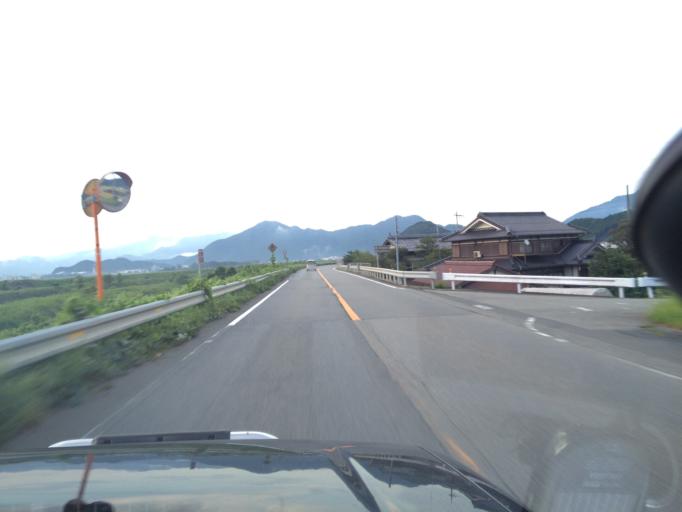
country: JP
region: Hyogo
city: Nishiwaki
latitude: 35.1422
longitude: 135.0288
